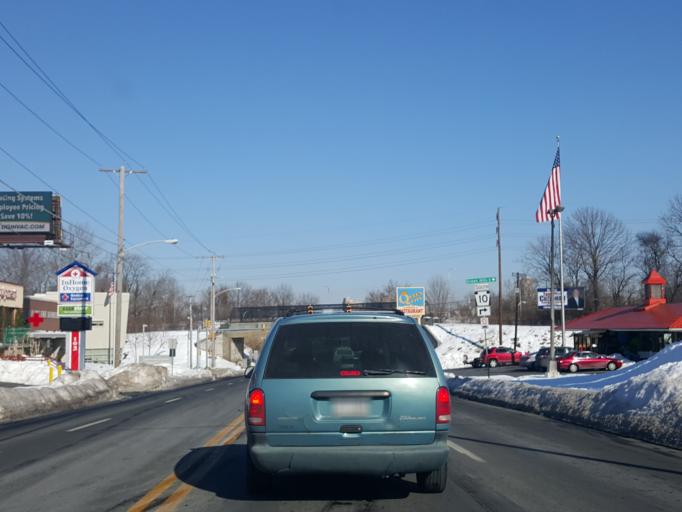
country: US
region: Pennsylvania
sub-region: Berks County
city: Kenhorst
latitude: 40.3226
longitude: -75.9341
